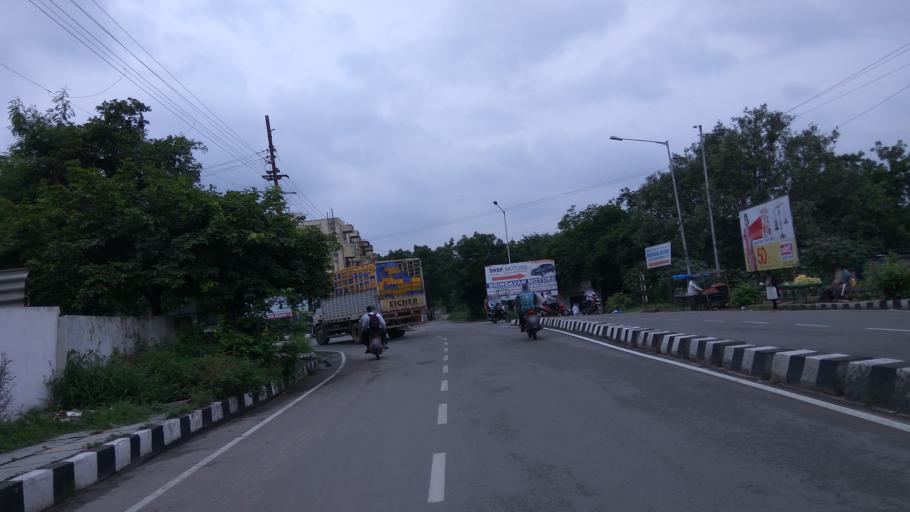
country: IN
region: Telangana
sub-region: Hyderabad
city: Malkajgiri
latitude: 17.4394
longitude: 78.5255
